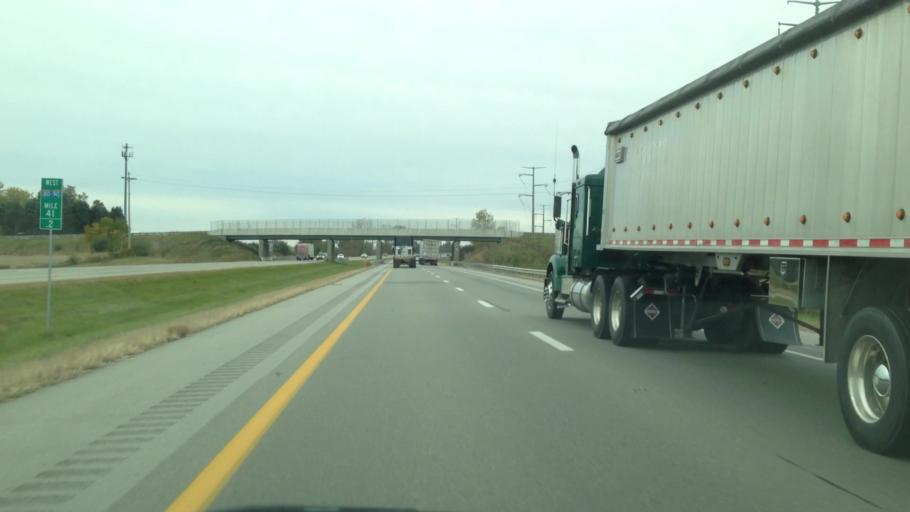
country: US
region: Ohio
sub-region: Fulton County
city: Delta
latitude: 41.5949
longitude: -84.0210
